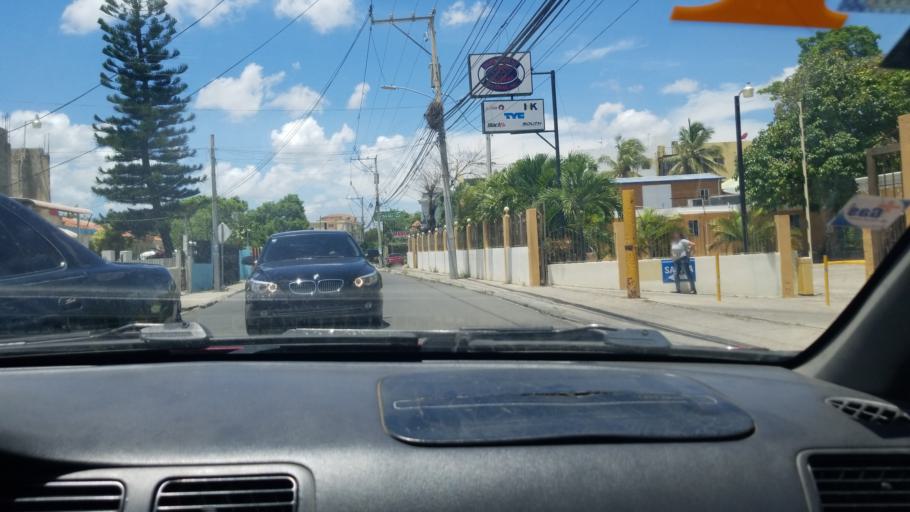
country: DO
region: Santiago
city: Santiago de los Caballeros
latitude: 19.4782
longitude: -70.6891
